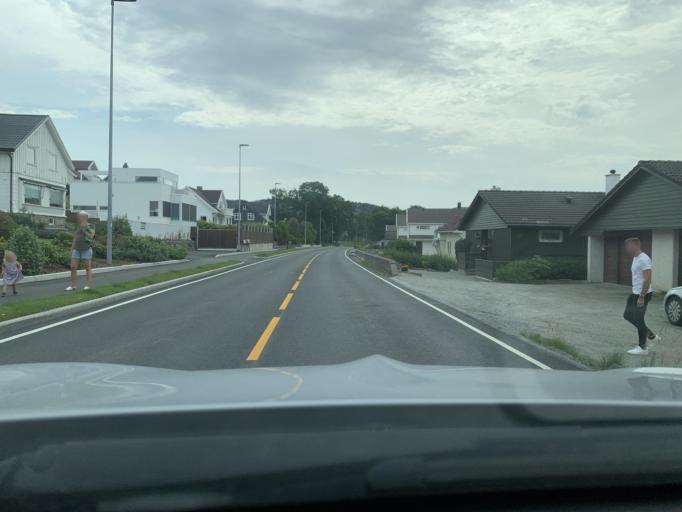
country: NO
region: Rogaland
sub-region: Sandnes
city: Sandnes
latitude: 58.7762
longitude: 5.7212
